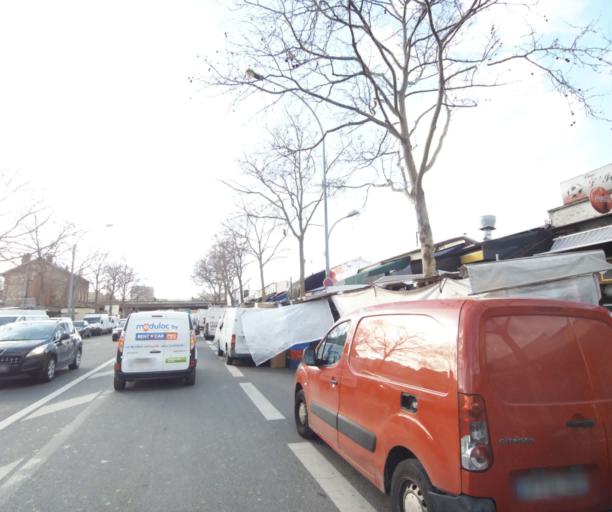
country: FR
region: Ile-de-France
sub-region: Paris
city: Saint-Ouen
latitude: 48.9025
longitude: 2.3441
